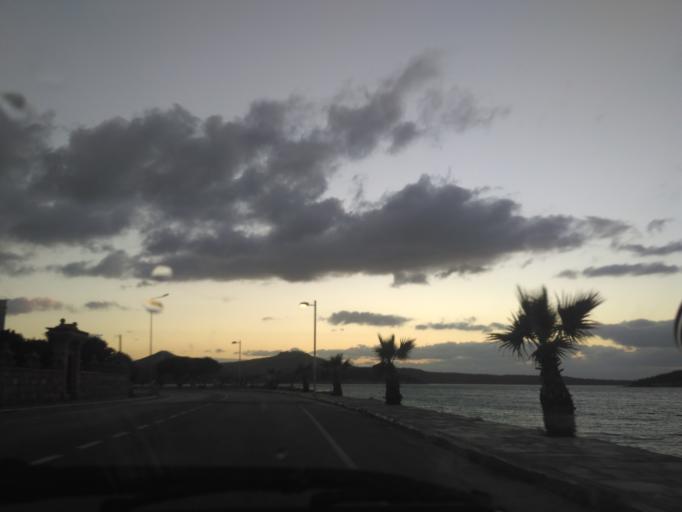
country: TR
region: Balikesir
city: Ayvalik
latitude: 39.3047
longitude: 26.6646
